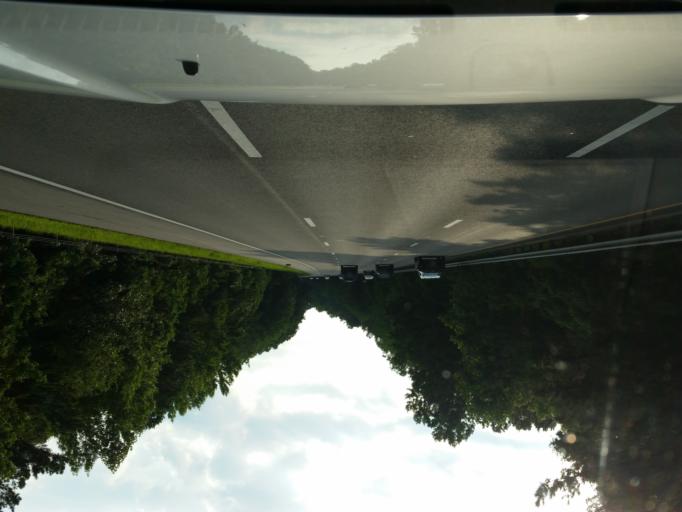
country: US
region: Virginia
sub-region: King William County
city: West Point
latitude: 37.4234
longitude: -76.8300
